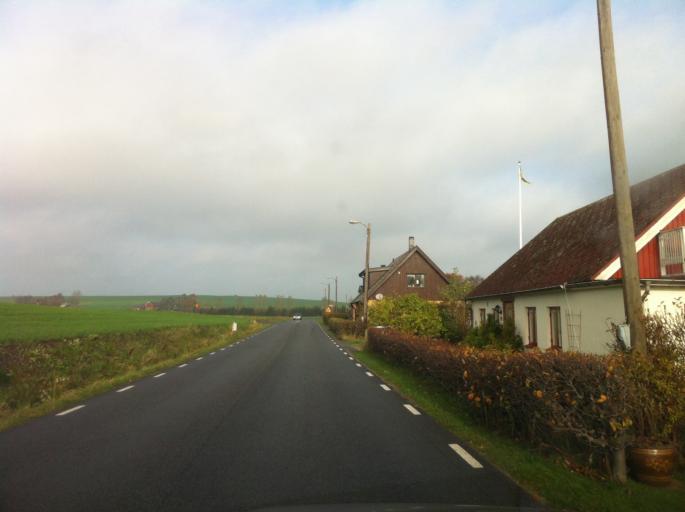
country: SE
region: Skane
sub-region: Landskrona
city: Asmundtorp
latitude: 55.9061
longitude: 12.9000
